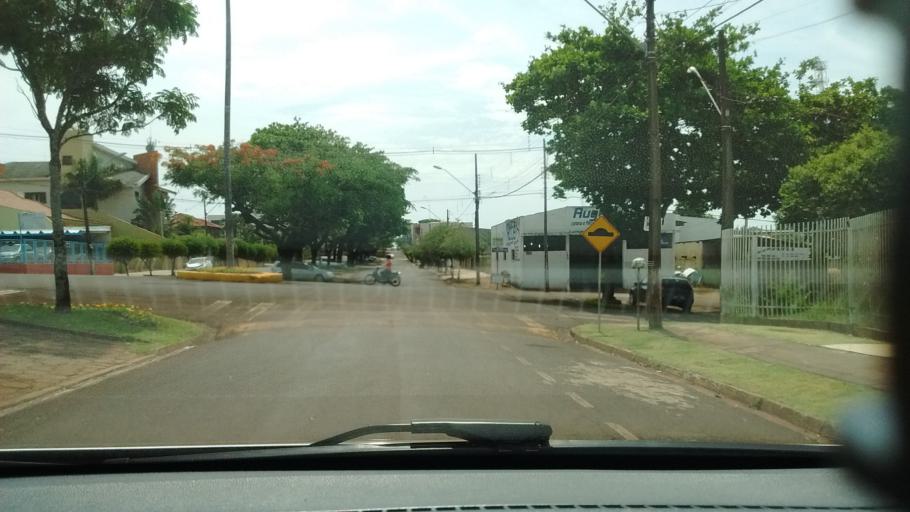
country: BR
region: Parana
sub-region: Corbelia
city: Corbelia
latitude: -24.5422
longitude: -52.9853
